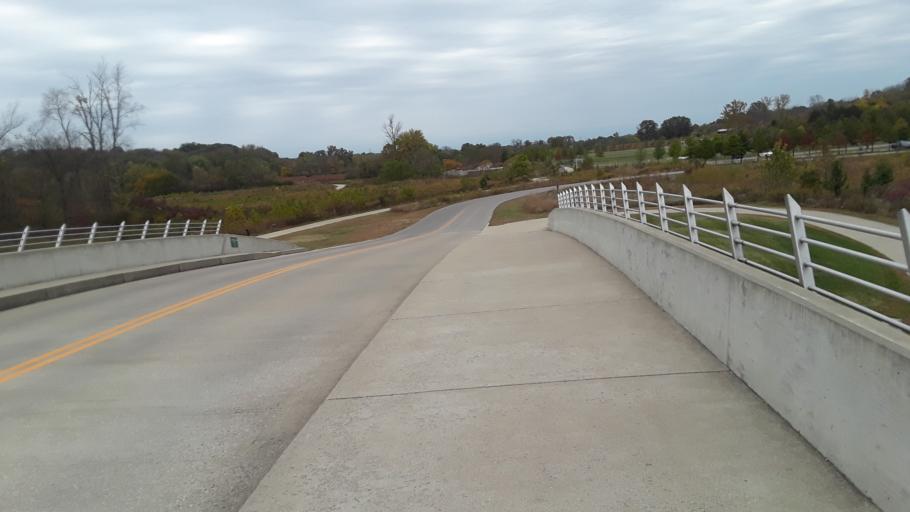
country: US
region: Kentucky
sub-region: Jefferson County
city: Middletown
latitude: 38.2075
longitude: -85.4745
